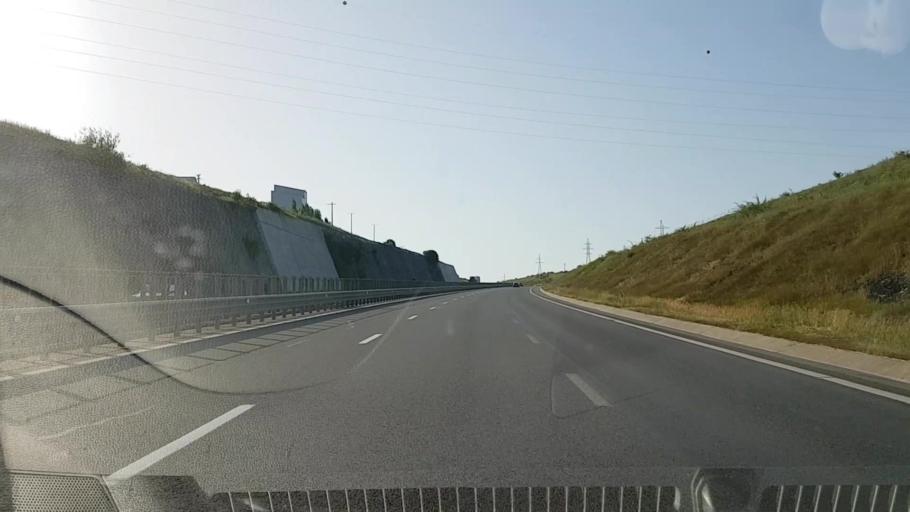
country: RO
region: Cluj
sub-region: Comuna Sandulesti
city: Sandulesti
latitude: 46.5959
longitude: 23.7116
